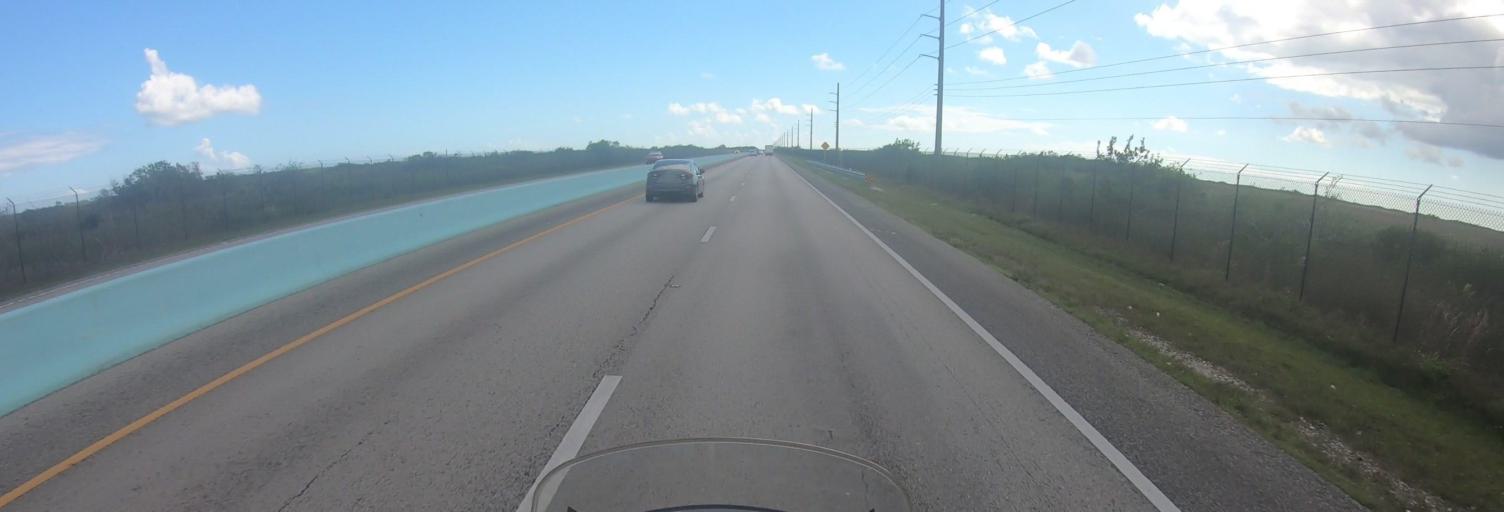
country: US
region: Florida
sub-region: Miami-Dade County
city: Florida City
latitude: 25.3493
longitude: -80.4579
